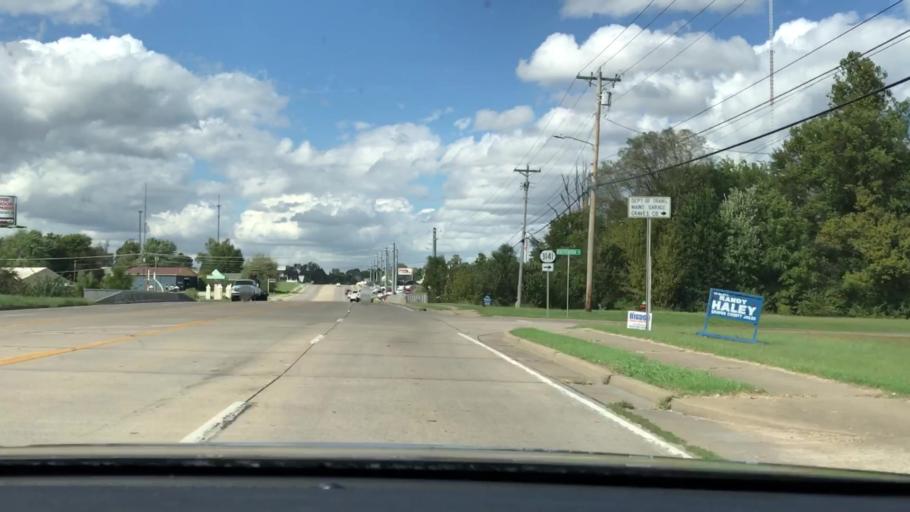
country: US
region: Kentucky
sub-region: Graves County
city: Mayfield
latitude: 36.7568
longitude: -88.6405
